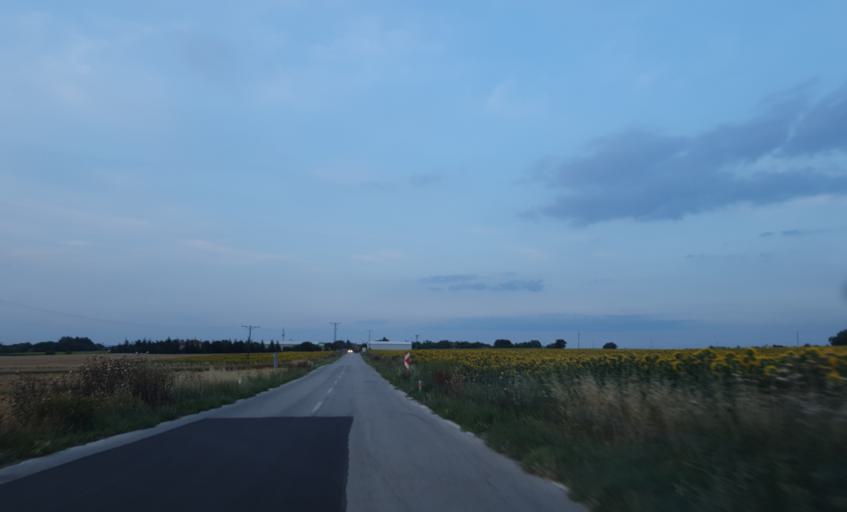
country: TR
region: Tekirdag
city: Beyazkoy
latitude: 41.4066
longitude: 27.6472
